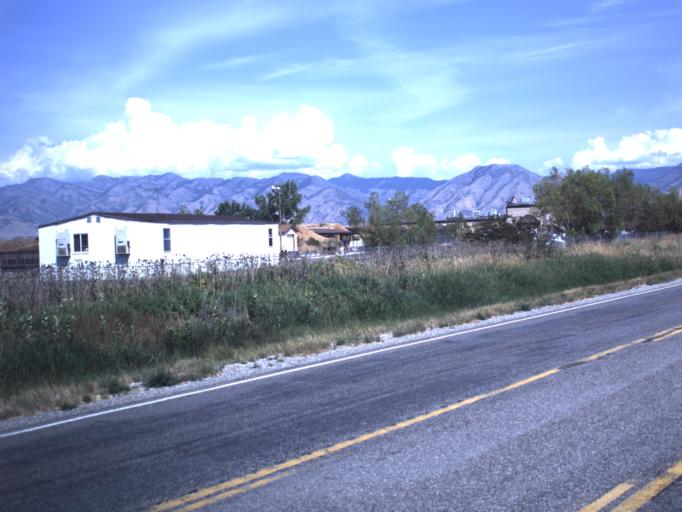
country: US
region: Utah
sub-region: Cache County
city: Benson
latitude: 41.7404
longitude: -111.9068
